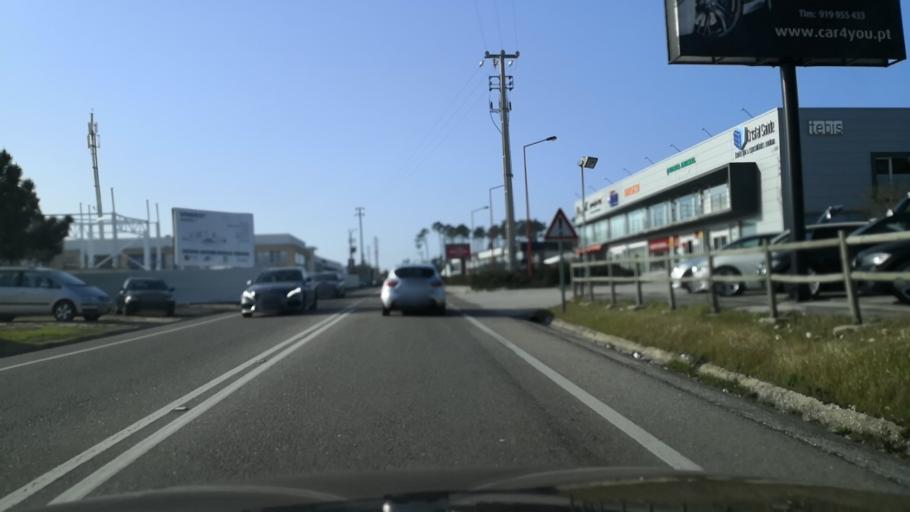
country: PT
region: Leiria
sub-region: Marinha Grande
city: Marinha Grande
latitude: 39.7460
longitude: -8.8965
